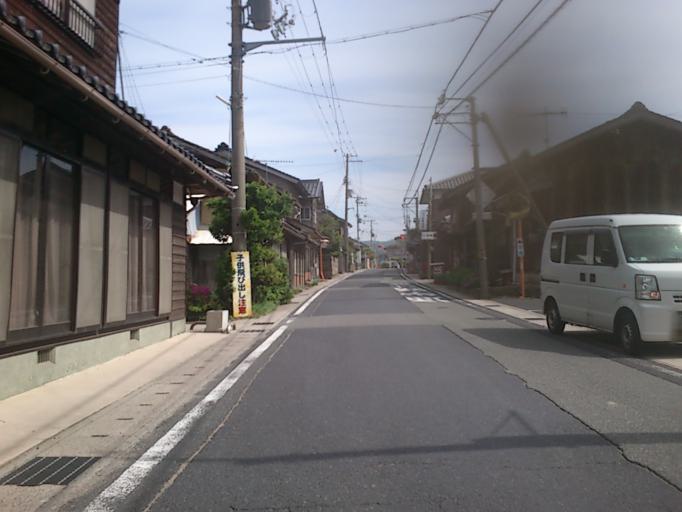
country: JP
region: Hyogo
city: Toyooka
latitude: 35.6641
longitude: 134.9683
